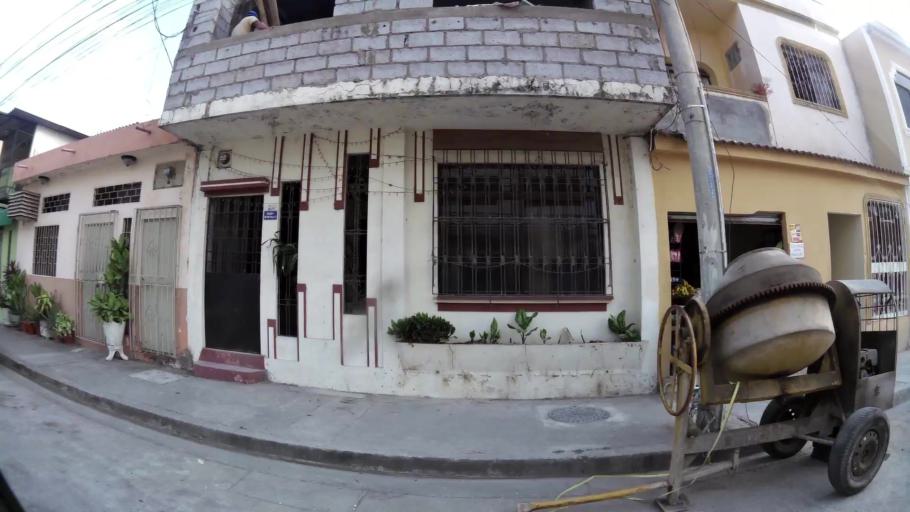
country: EC
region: Guayas
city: Eloy Alfaro
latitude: -2.1357
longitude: -79.8918
